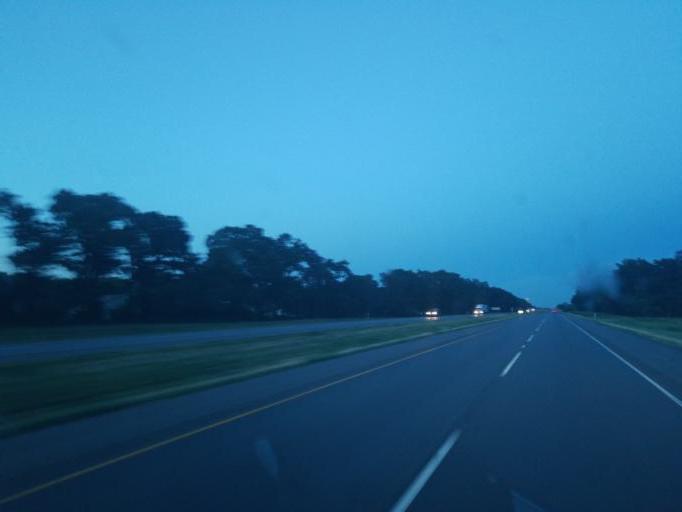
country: US
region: Indiana
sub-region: Saint Joseph County
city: Georgetown
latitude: 41.7159
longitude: -86.2103
